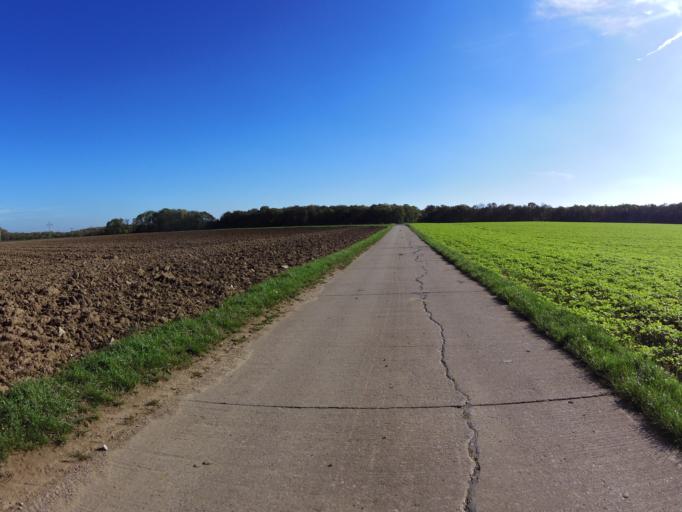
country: DE
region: Bavaria
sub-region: Regierungsbezirk Unterfranken
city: Biebelried
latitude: 49.7258
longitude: 10.0938
